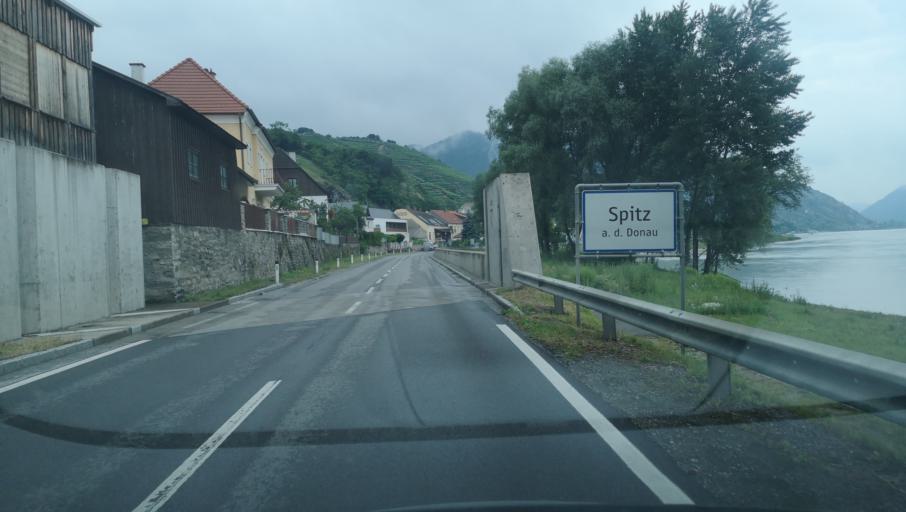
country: AT
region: Lower Austria
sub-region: Politischer Bezirk Krems
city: Spitz
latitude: 48.3565
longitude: 15.4084
